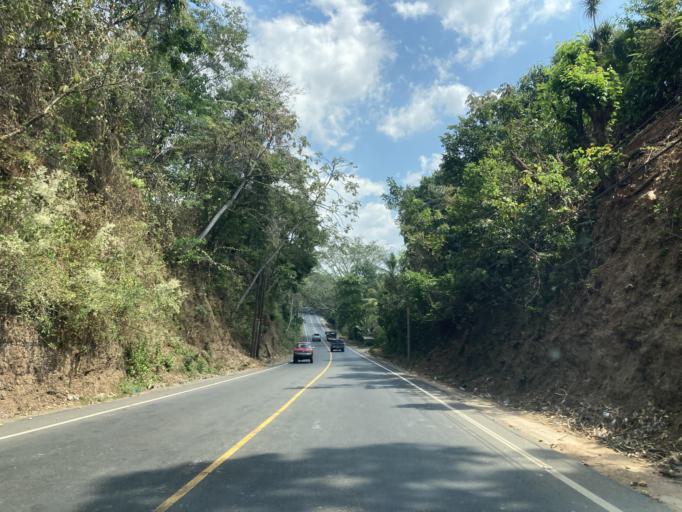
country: GT
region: Santa Rosa
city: Guazacapan
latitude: 14.0679
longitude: -90.4378
